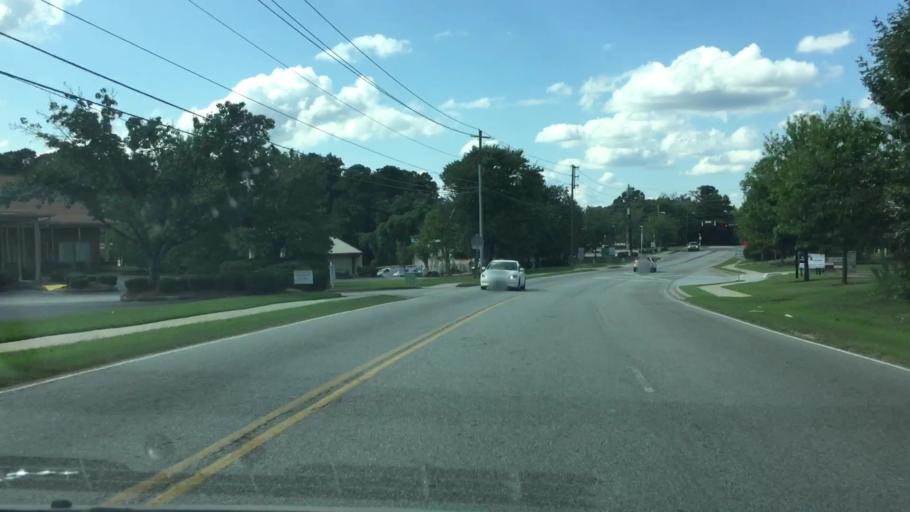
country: US
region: Georgia
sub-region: Fayette County
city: Fayetteville
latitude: 33.4451
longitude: -84.4672
